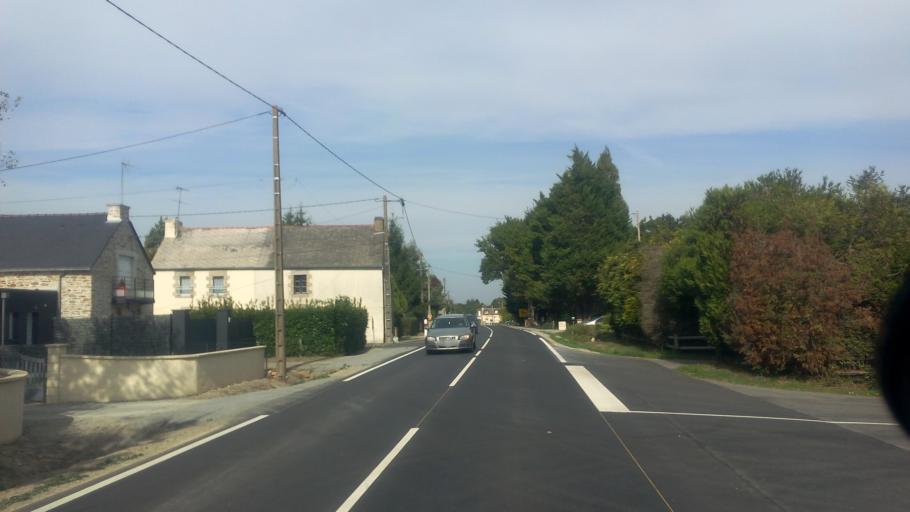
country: FR
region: Brittany
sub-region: Departement d'Ille-et-Vilaine
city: Bains-sur-Oust
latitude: 47.6977
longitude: -2.0847
